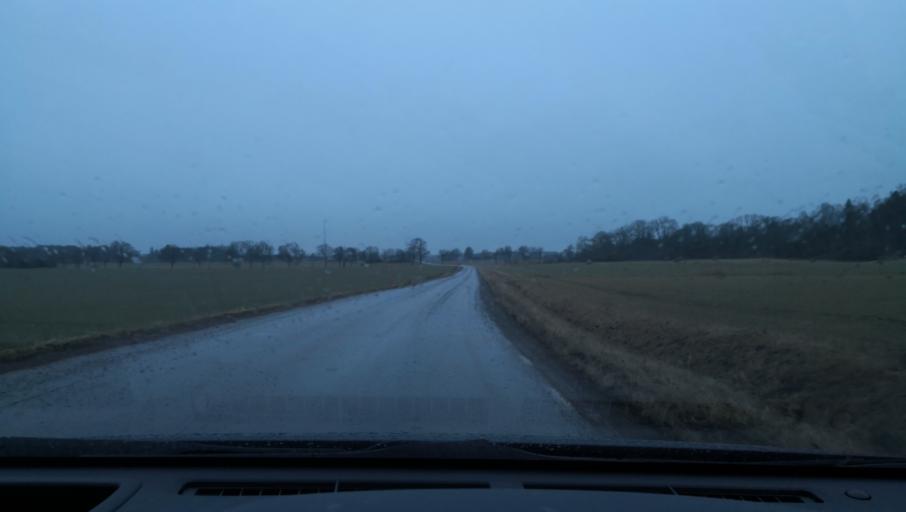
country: SE
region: Soedermanland
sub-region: Eskilstuna Kommun
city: Arla
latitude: 59.4475
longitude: 16.7233
